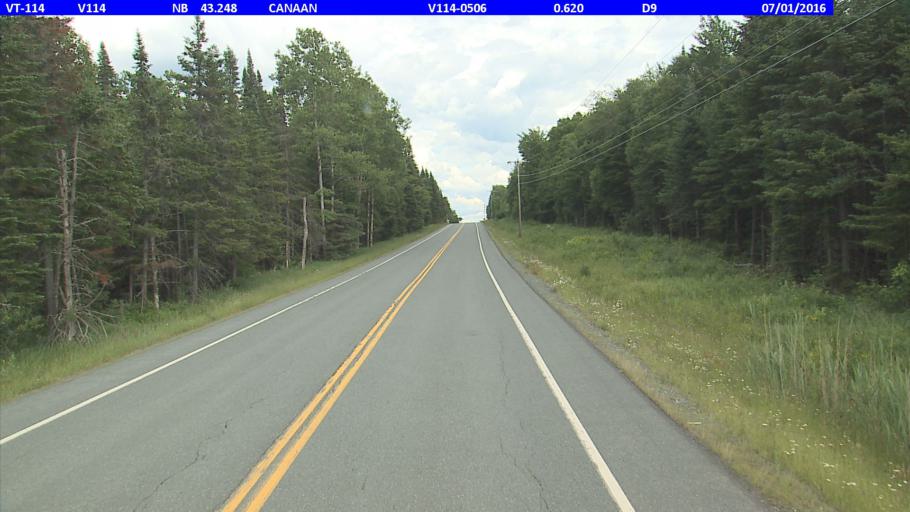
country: CA
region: Quebec
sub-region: Estrie
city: Coaticook
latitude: 45.0063
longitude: -71.6812
